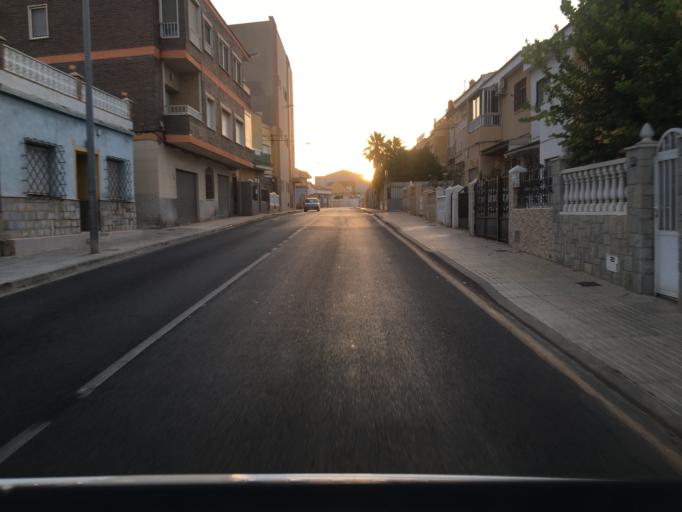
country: ES
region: Murcia
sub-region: Murcia
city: Cartagena
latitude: 37.6281
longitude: -1.0001
